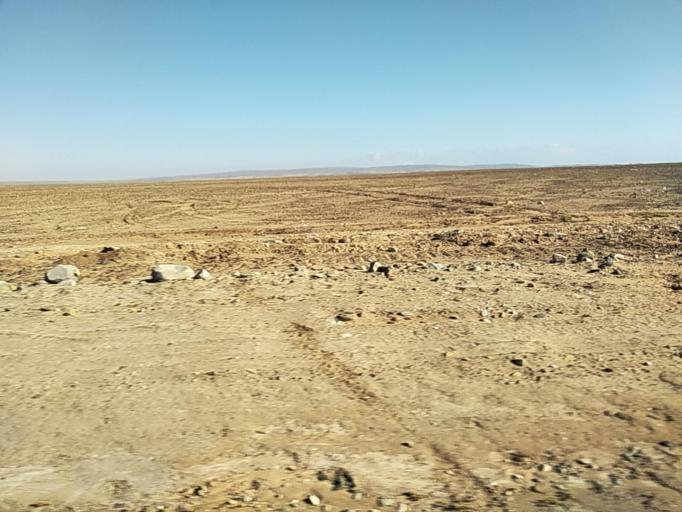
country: CL
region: Atacama
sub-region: Provincia de Copiapo
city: Copiapo
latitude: -27.3166
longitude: -70.8626
